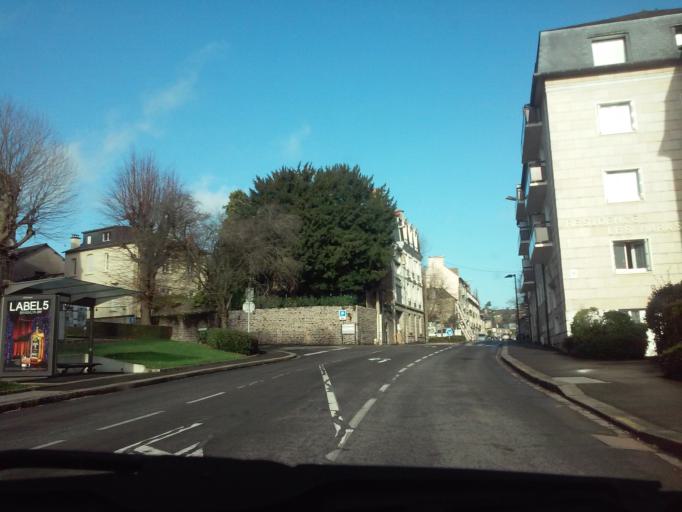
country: FR
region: Brittany
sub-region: Departement d'Ille-et-Vilaine
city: Fougeres
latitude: 48.3466
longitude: -1.2024
